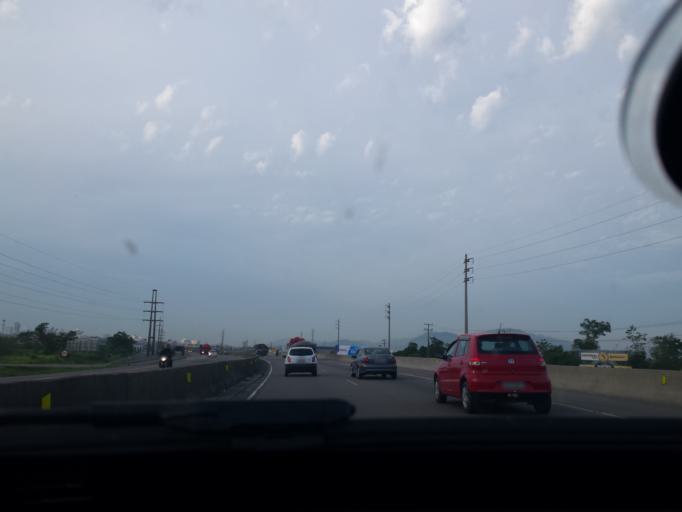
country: BR
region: Santa Catarina
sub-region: Tubarao
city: Tubarao
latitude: -28.4601
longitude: -48.9896
